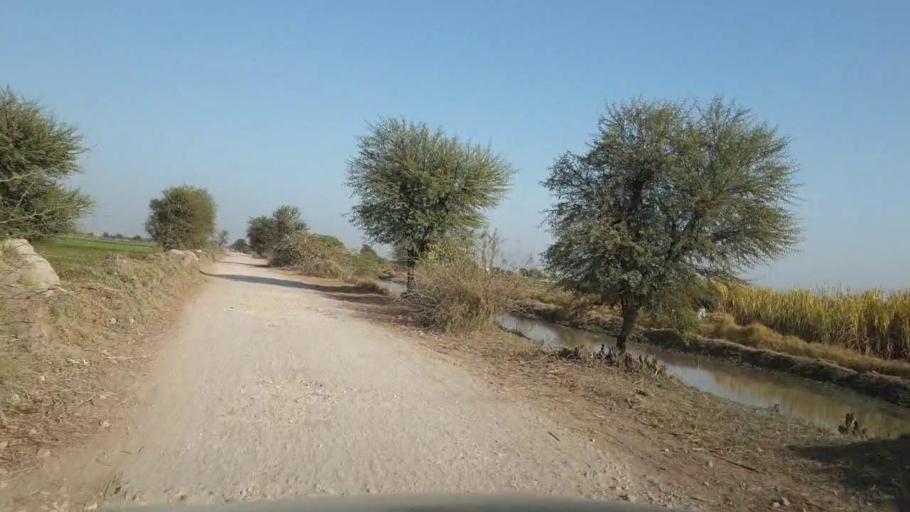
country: PK
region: Sindh
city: Tando Allahyar
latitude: 25.5932
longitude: 68.6658
